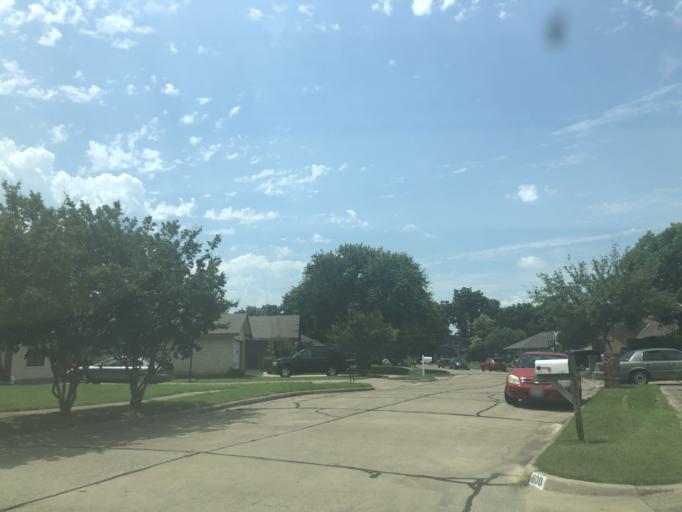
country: US
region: Texas
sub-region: Dallas County
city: Irving
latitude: 32.7899
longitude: -96.9369
